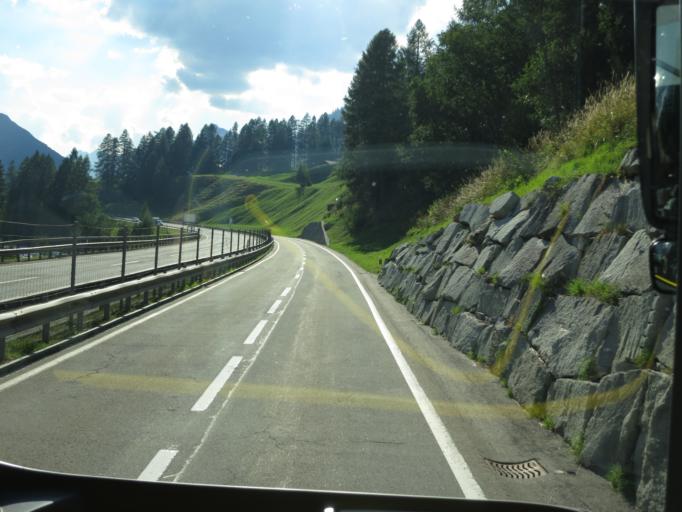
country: CH
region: Grisons
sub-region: Hinterrhein District
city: Hinterrhein
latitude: 46.5472
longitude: 9.3060
